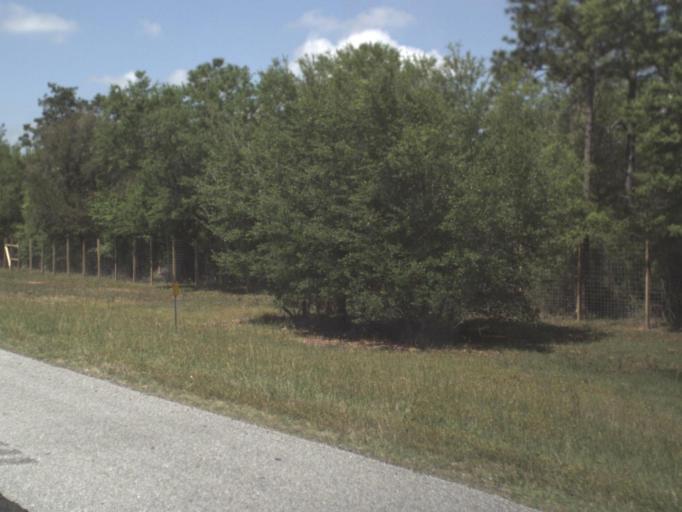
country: US
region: Florida
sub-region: Santa Rosa County
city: East Milton
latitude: 30.5992
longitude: -86.9936
